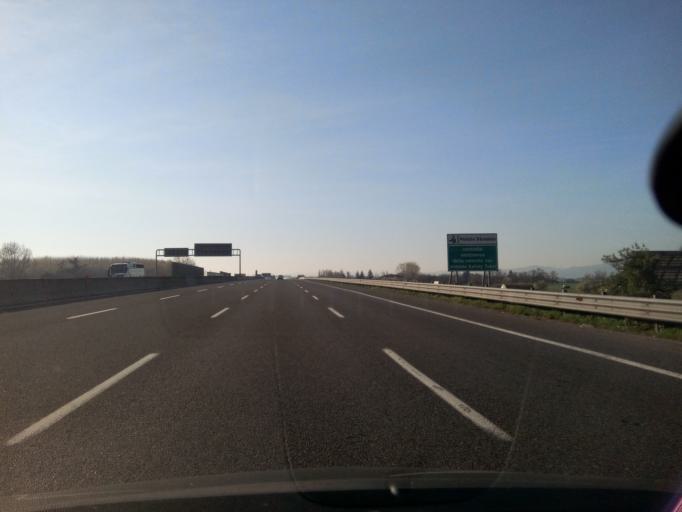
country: IT
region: Emilia-Romagna
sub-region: Provincia di Modena
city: Campogalliano
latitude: 44.6521
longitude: 10.8639
